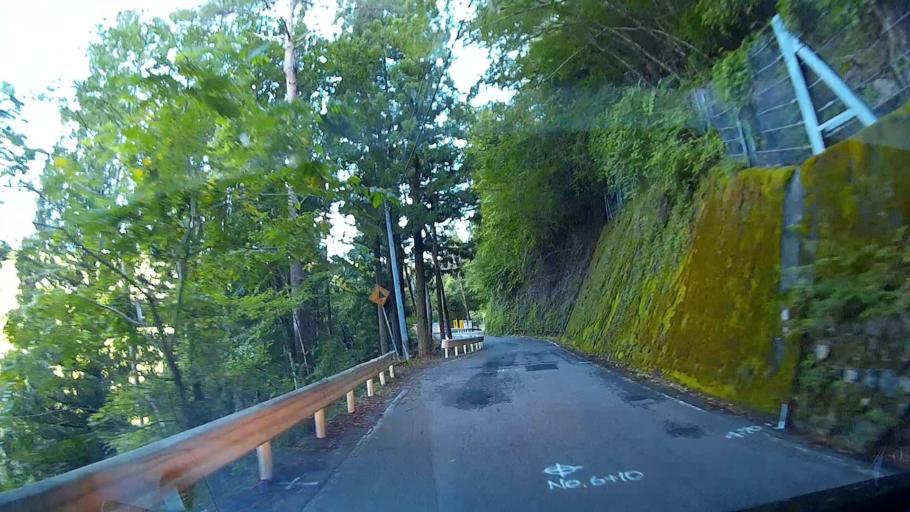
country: JP
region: Shizuoka
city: Shizuoka-shi
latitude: 35.2072
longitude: 138.2348
